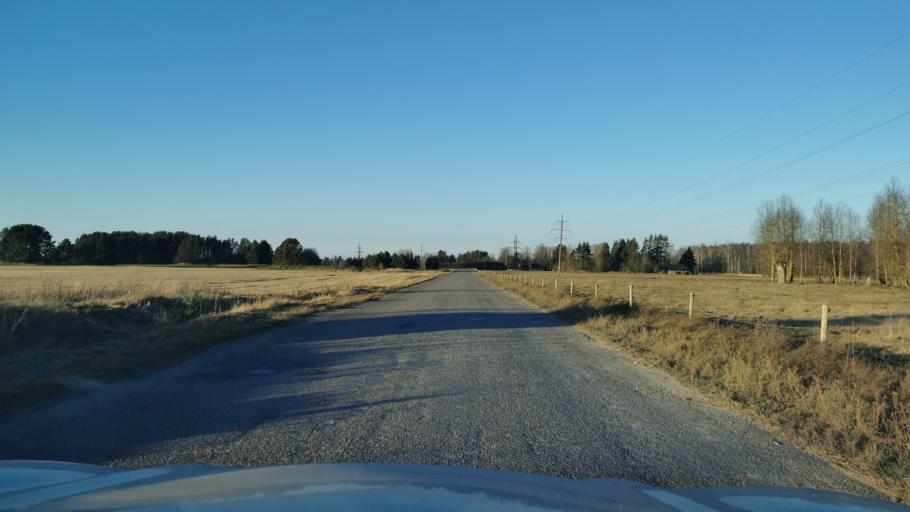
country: EE
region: Ida-Virumaa
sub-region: Puessi linn
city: Pussi
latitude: 59.3417
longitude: 27.0524
